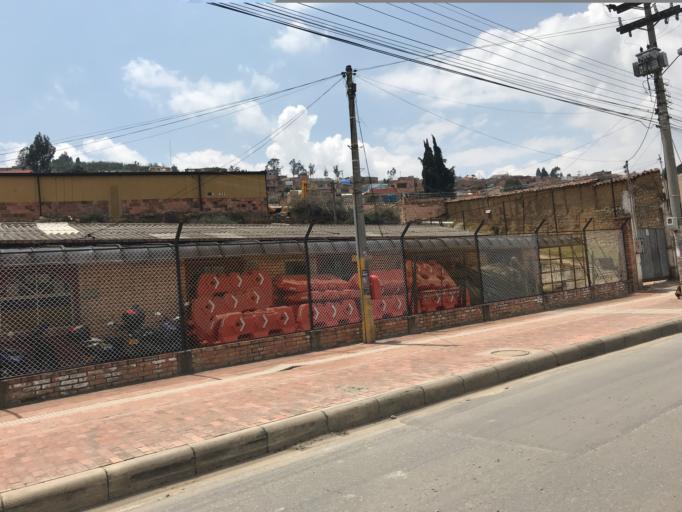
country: CO
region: Boyaca
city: Tunja
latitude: 5.5384
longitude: -73.3679
